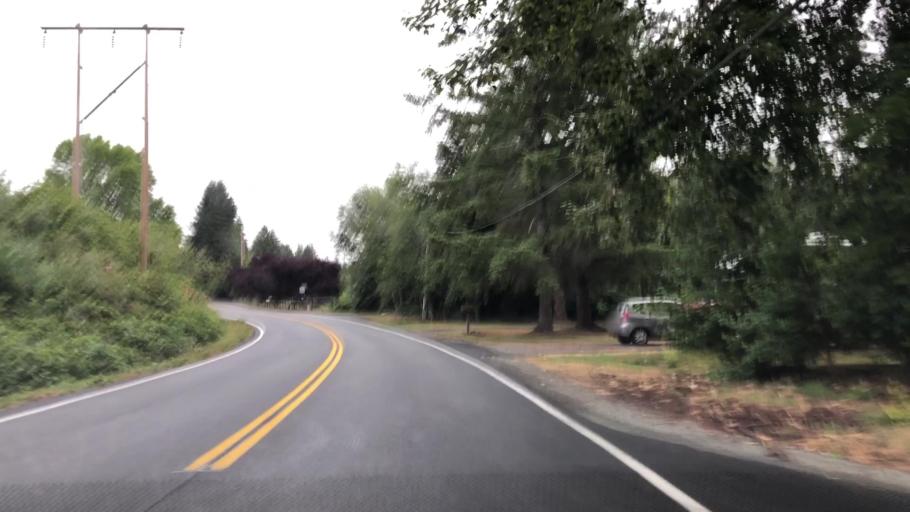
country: US
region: Washington
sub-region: Snohomish County
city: North Creek
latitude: 47.8238
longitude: -122.2028
